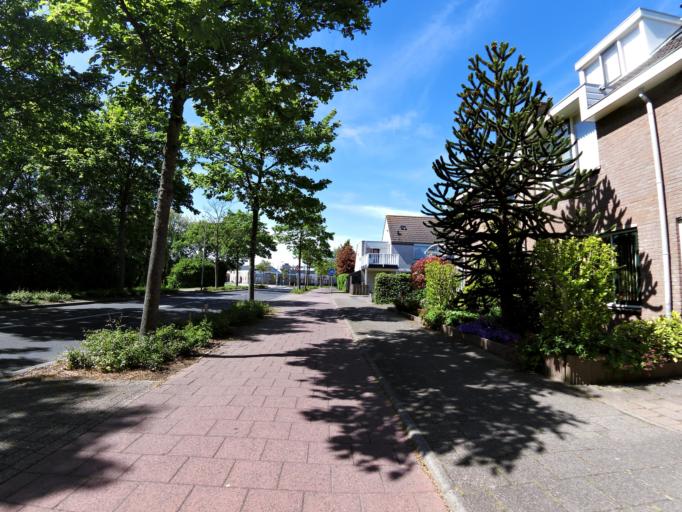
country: NL
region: South Holland
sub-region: Gemeente Hellevoetsluis
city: Nieuwenhoorn
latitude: 51.8415
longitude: 4.1541
